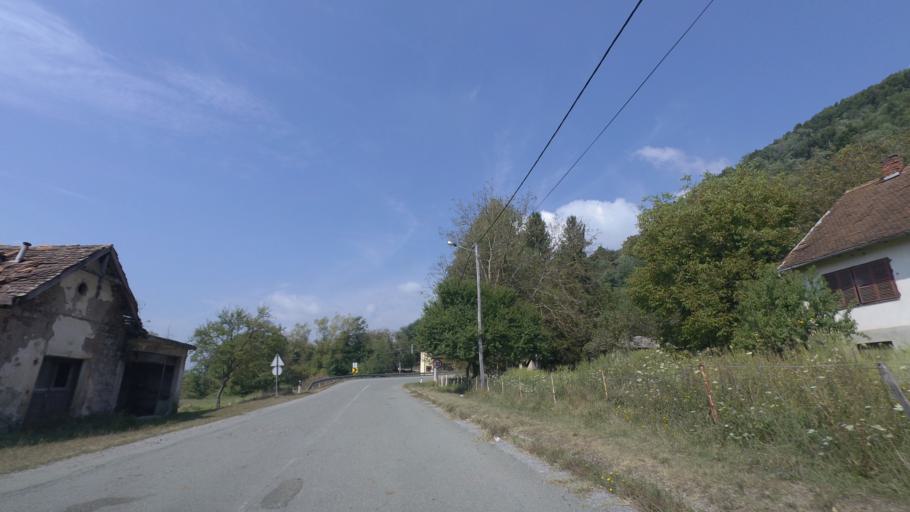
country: BA
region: Federation of Bosnia and Herzegovina
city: Zboriste
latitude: 45.1511
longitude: 16.1437
